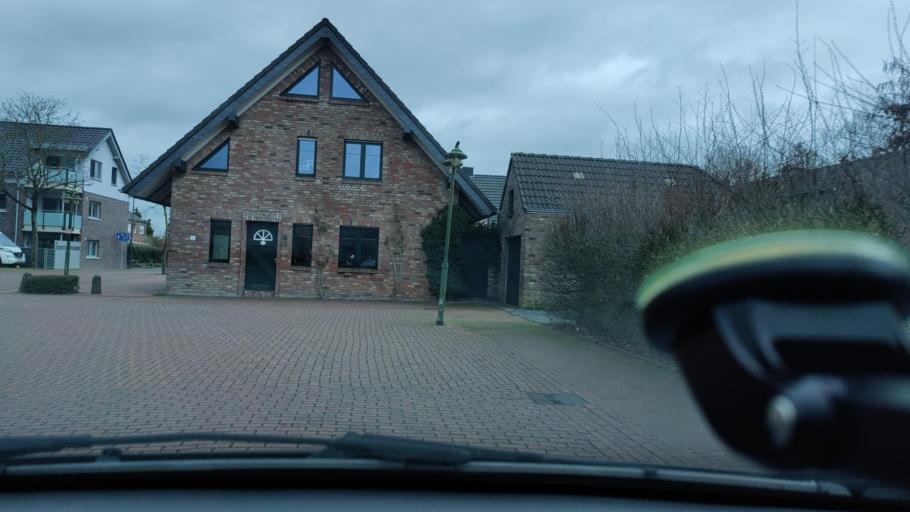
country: DE
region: North Rhine-Westphalia
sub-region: Regierungsbezirk Dusseldorf
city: Kevelaer
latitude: 51.5537
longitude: 6.2118
